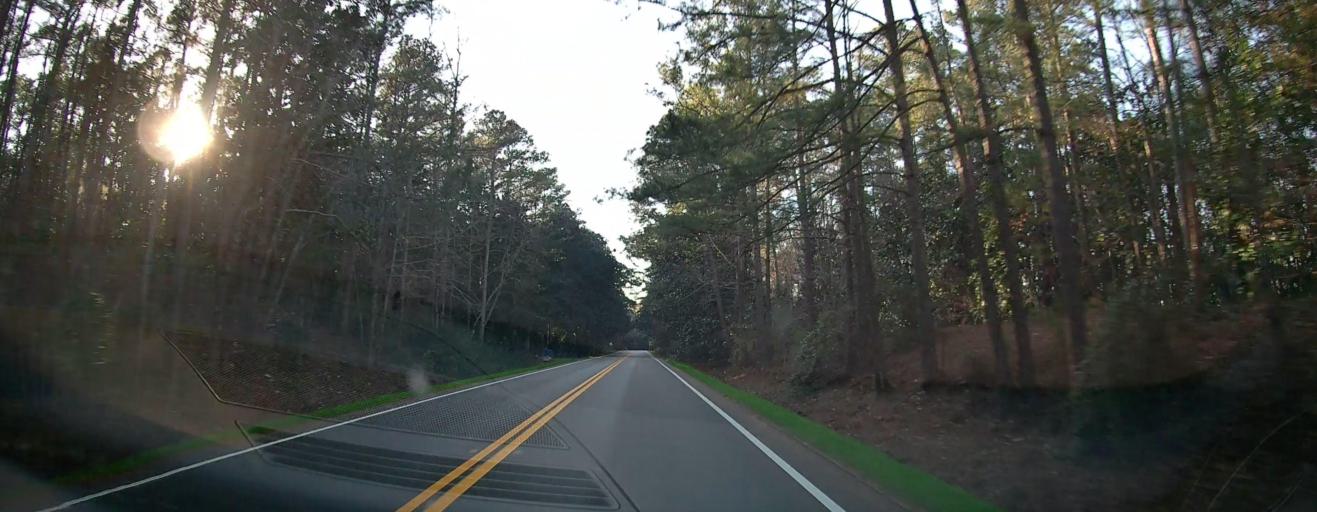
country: US
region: Georgia
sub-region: Harris County
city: Hamilton
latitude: 32.7497
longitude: -84.9233
